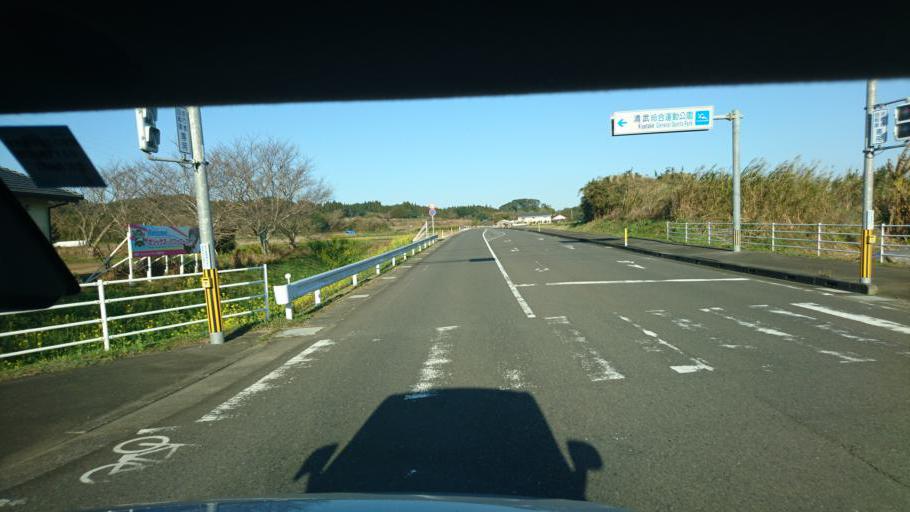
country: JP
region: Miyazaki
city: Miyazaki-shi
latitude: 31.8513
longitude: 131.3775
